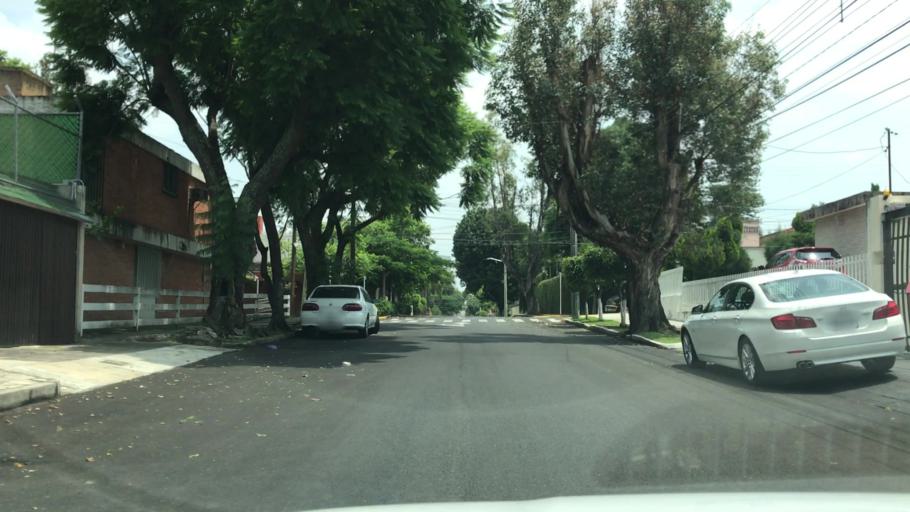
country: MX
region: Jalisco
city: Guadalajara
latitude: 20.6561
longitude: -103.4050
